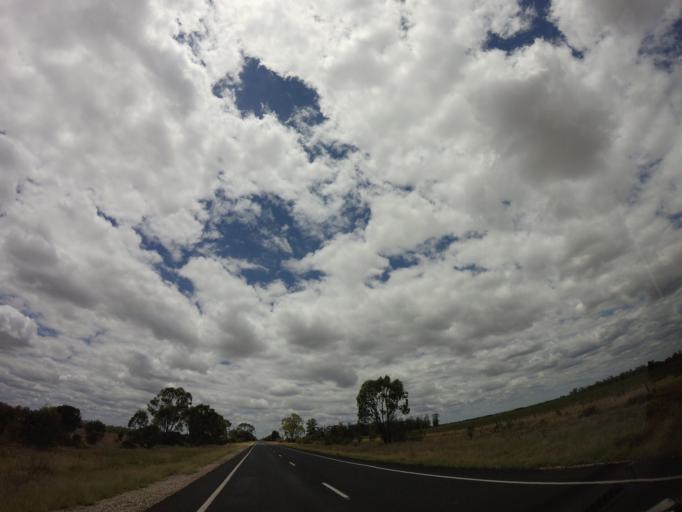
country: AU
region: Queensland
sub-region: Goondiwindi
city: Goondiwindi
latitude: -28.1756
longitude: 150.4830
